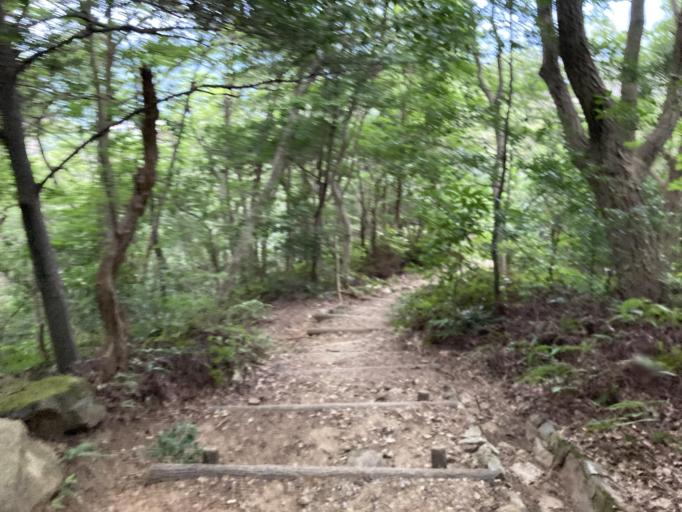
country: JP
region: Aichi
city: Nishio
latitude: 34.8476
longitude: 137.1206
